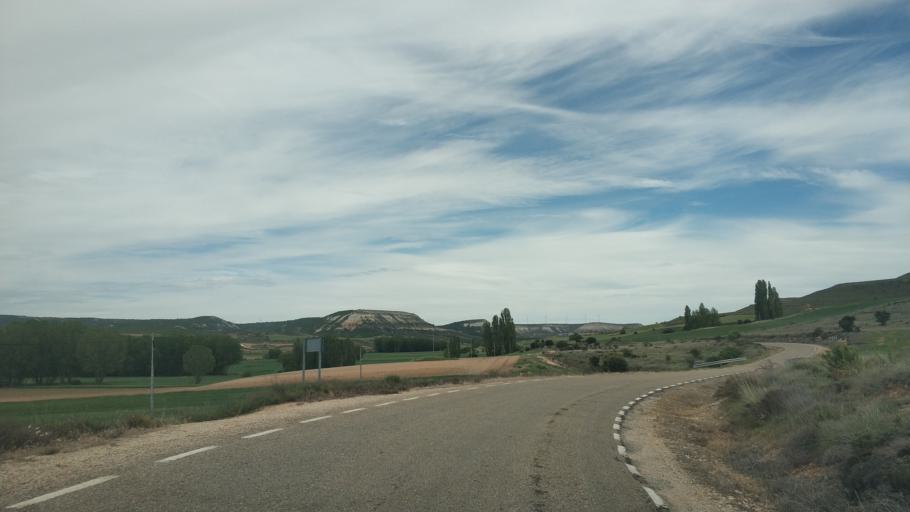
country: ES
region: Castille and Leon
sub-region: Provincia de Soria
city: Caltojar
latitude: 41.4352
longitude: -2.8080
